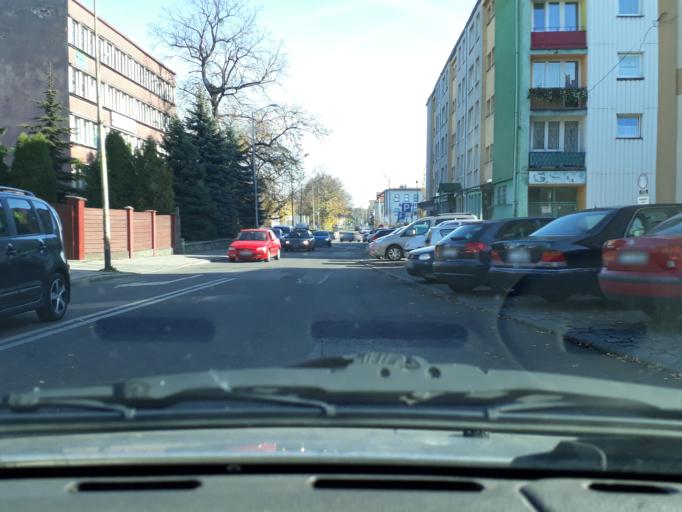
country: PL
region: Silesian Voivodeship
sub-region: Powiat tarnogorski
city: Tarnowskie Gory
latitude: 50.4432
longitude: 18.8607
